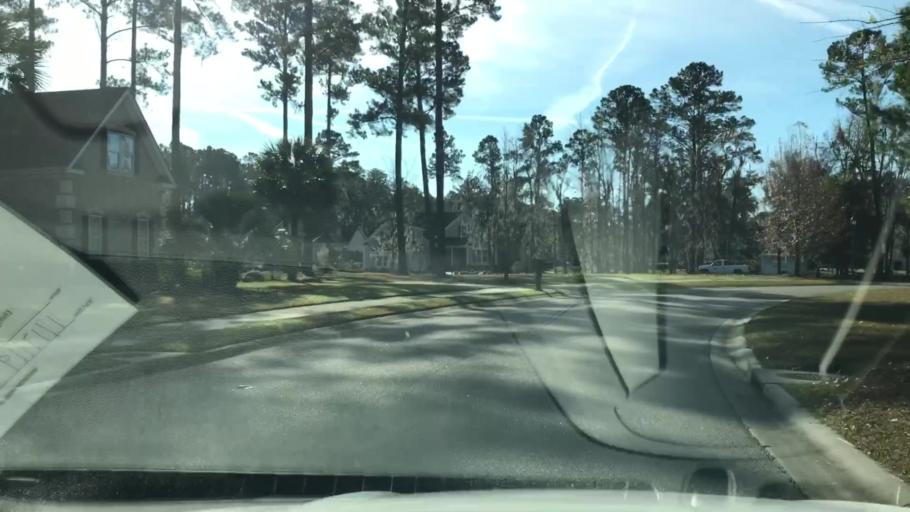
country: US
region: South Carolina
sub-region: Beaufort County
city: Bluffton
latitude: 32.2442
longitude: -80.9131
